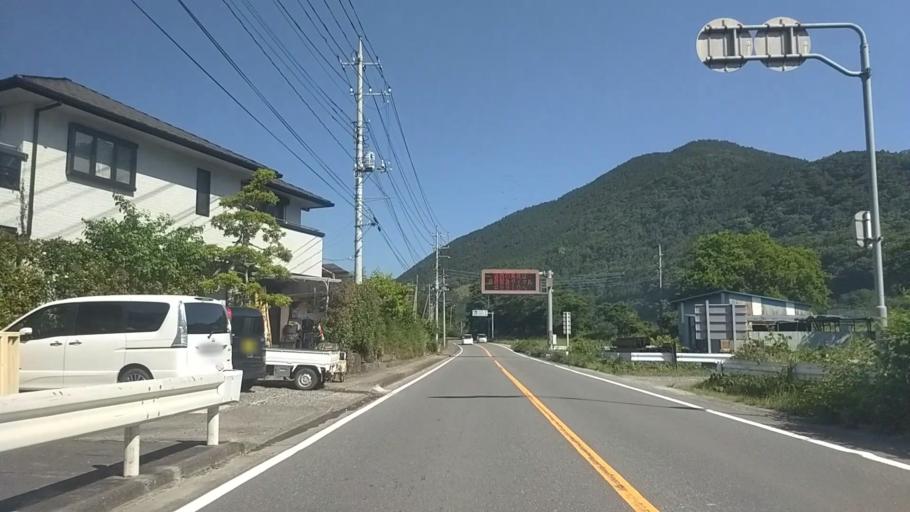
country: JP
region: Shizuoka
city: Fujinomiya
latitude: 35.2368
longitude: 138.5052
